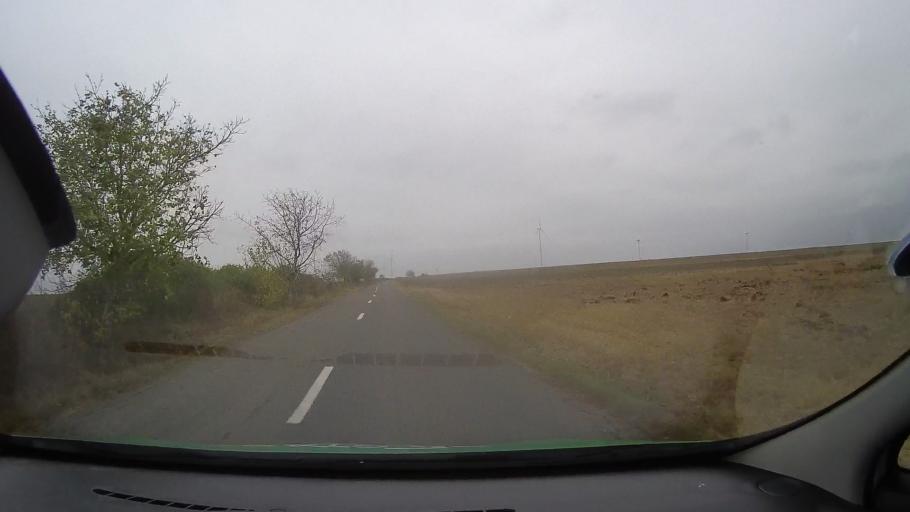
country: RO
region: Constanta
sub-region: Comuna Pantelimon
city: Pantelimon
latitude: 44.5006
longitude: 28.3559
